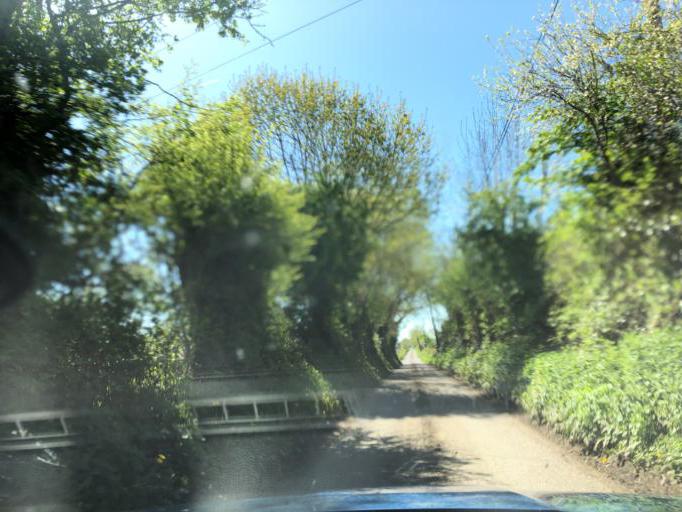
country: IE
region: Connaught
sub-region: County Galway
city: Portumna
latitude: 53.1479
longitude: -8.3394
